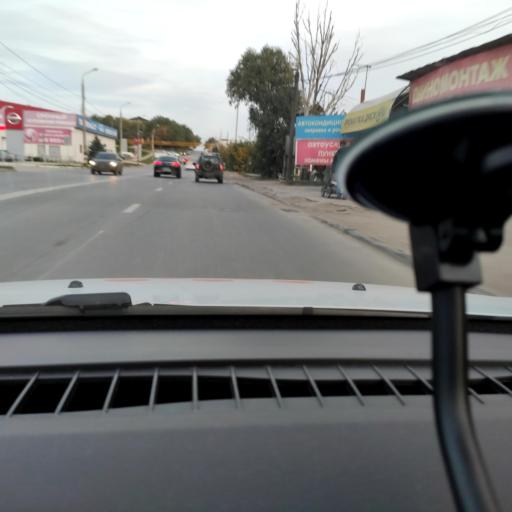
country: RU
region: Samara
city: Samara
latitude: 53.1827
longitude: 50.1507
